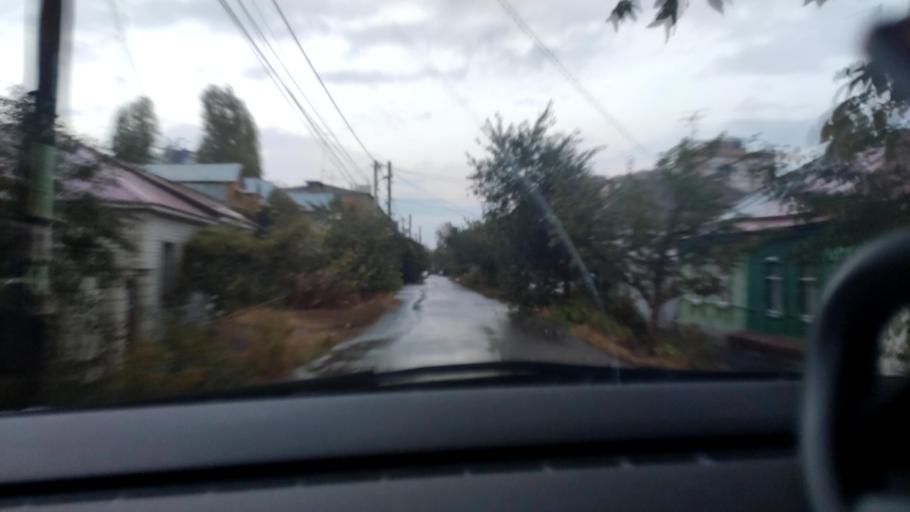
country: RU
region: Voronezj
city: Voronezh
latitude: 51.6936
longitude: 39.1754
